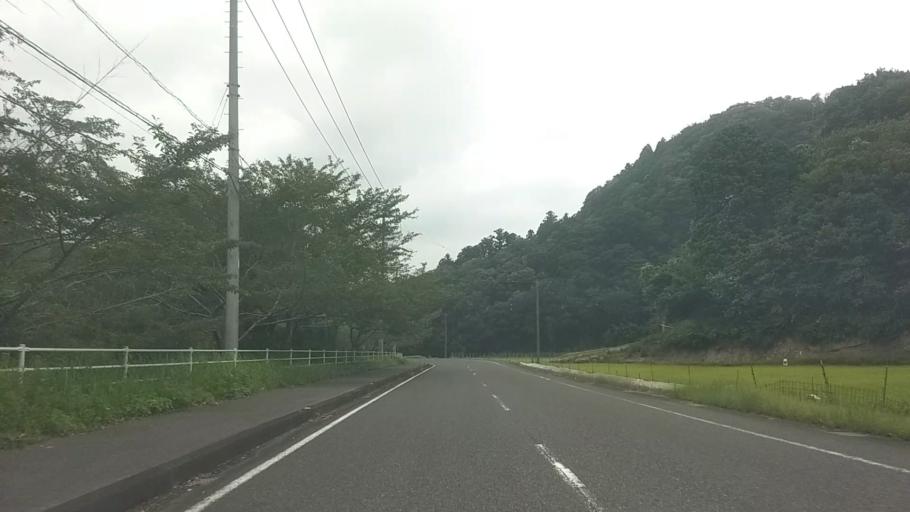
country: JP
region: Chiba
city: Kawaguchi
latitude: 35.2444
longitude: 140.0375
